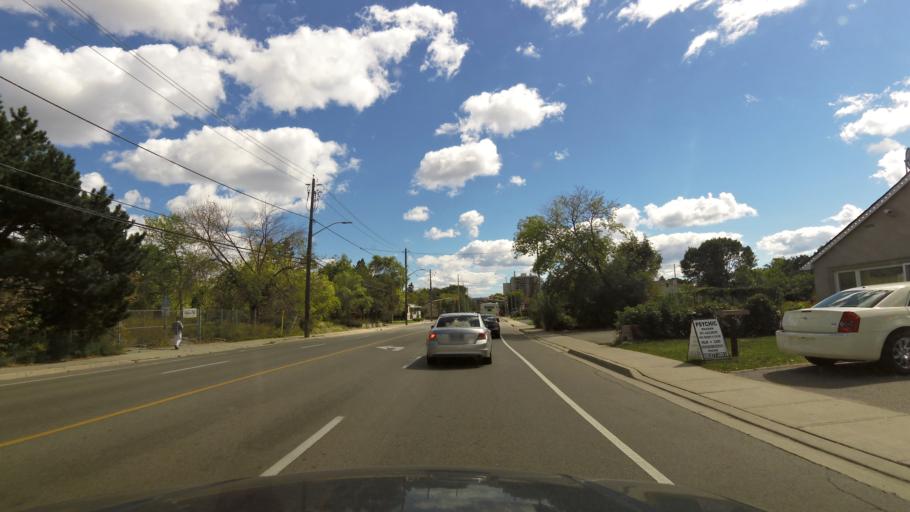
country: CA
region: Ontario
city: Mississauga
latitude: 43.5768
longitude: -79.6181
